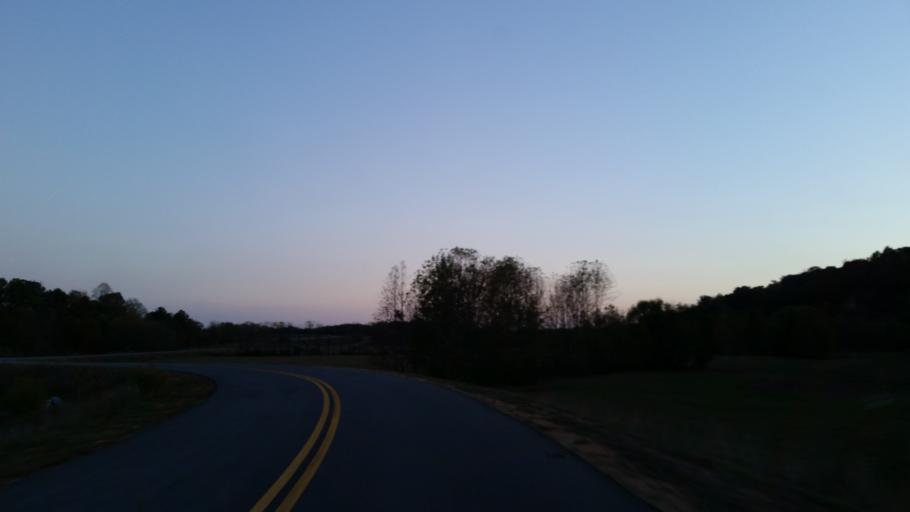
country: US
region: Georgia
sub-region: Gordon County
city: Calhoun
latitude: 34.5853
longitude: -84.9544
